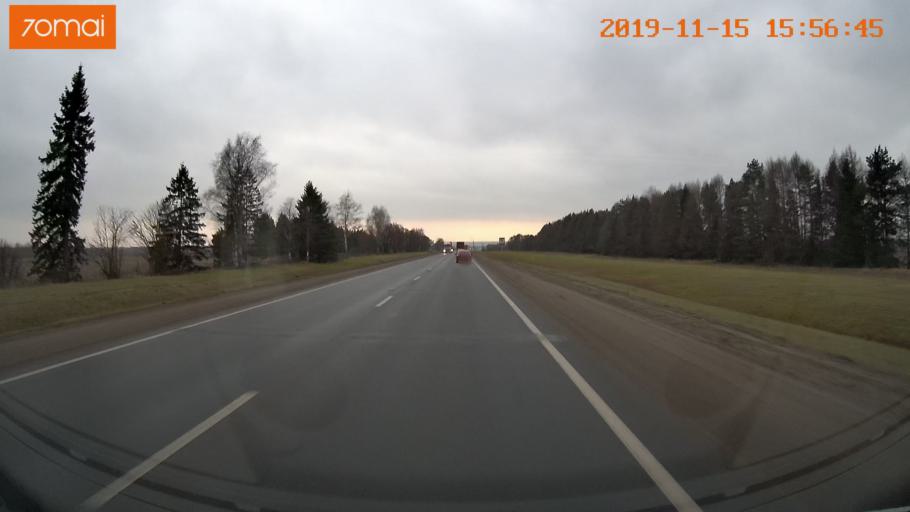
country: RU
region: Jaroslavl
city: Yaroslavl
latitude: 57.8384
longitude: 39.9701
